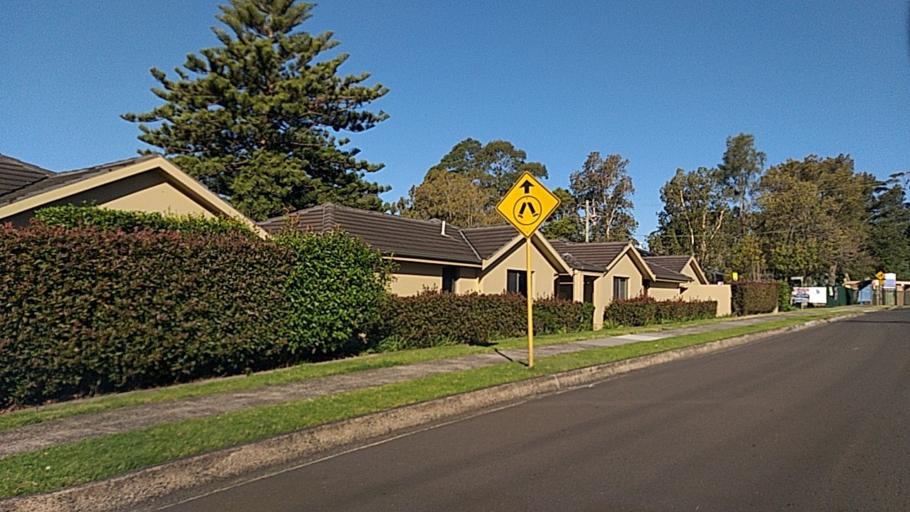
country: AU
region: New South Wales
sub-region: Wollongong
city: Corrimal
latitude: -34.3791
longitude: 150.8887
